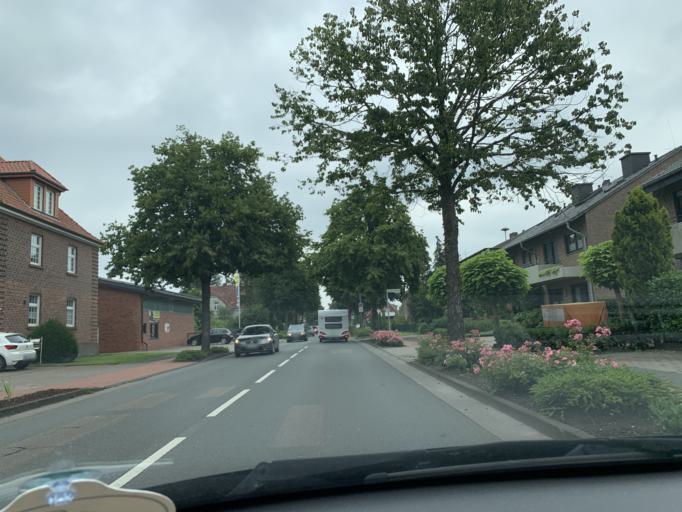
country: DE
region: North Rhine-Westphalia
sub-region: Regierungsbezirk Munster
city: Ostbevern
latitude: 52.0375
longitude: 7.8474
